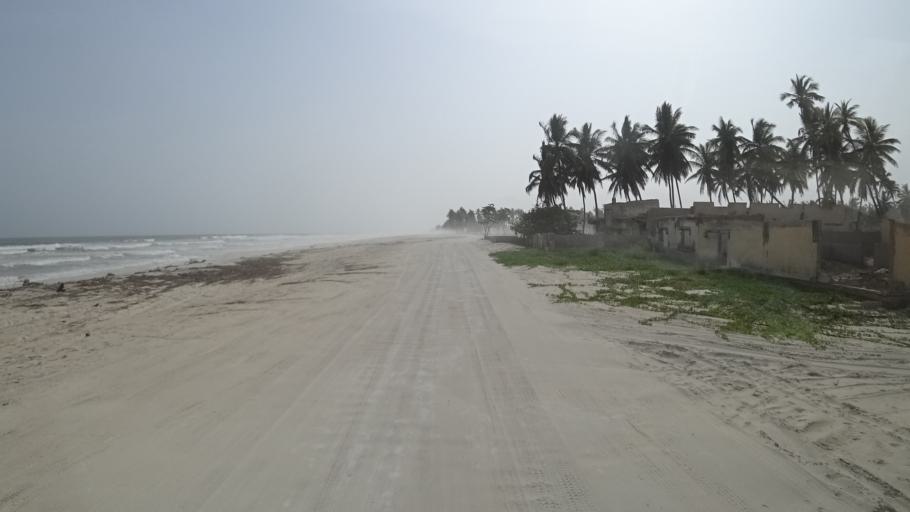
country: OM
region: Zufar
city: Salalah
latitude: 17.0028
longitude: 54.1231
